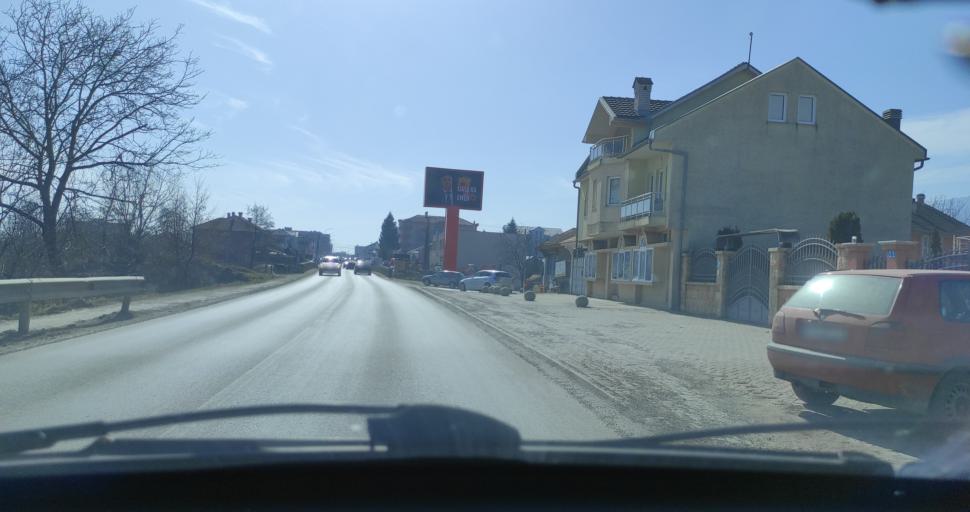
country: XK
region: Gjakova
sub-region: Komuna e Decanit
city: Decan
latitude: 42.5498
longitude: 20.2905
